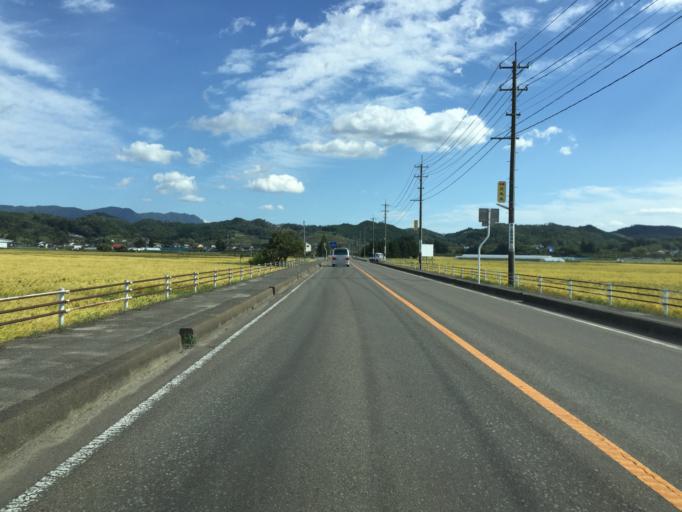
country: JP
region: Fukushima
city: Hobaramachi
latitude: 37.8120
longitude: 140.5639
